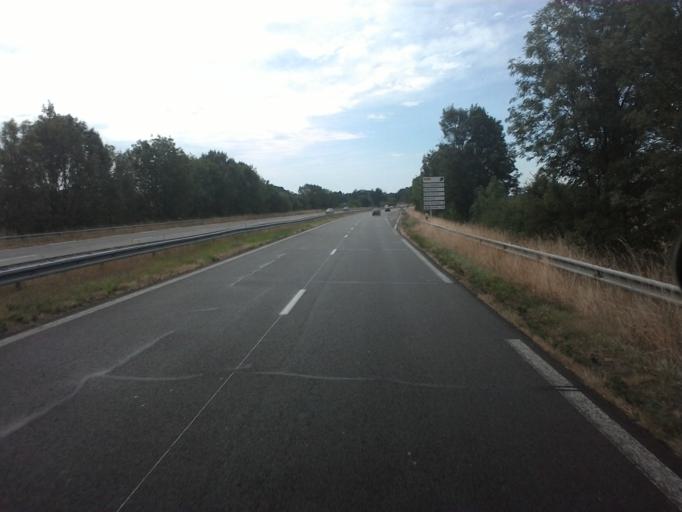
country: FR
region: Franche-Comte
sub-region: Departement du Jura
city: Montmorot
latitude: 46.7628
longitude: 5.5558
